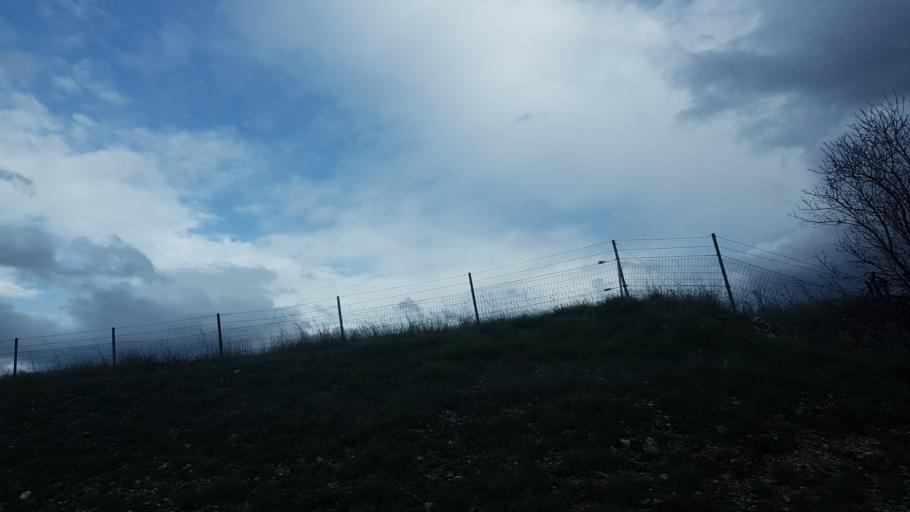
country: IT
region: Abruzzo
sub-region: Provincia dell' Aquila
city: Progetto Case Bazzano
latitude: 42.3664
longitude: 13.4297
